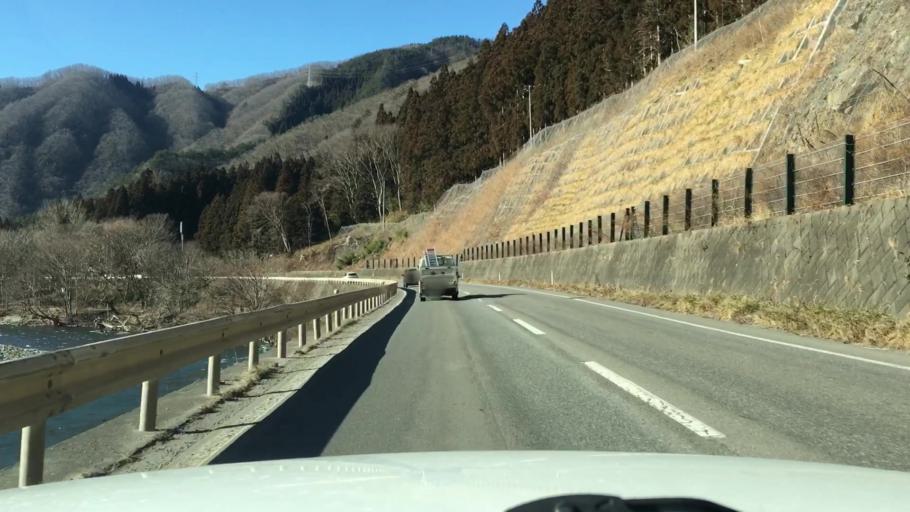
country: JP
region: Iwate
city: Miyako
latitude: 39.6272
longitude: 141.8225
